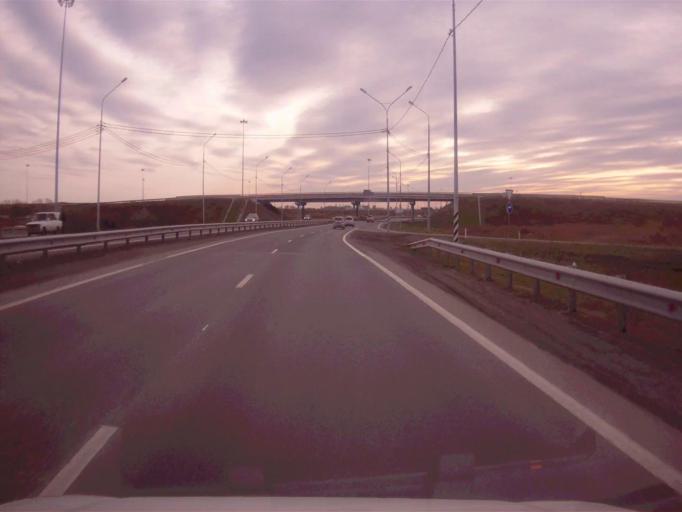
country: RU
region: Chelyabinsk
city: Novosineglazovskiy
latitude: 55.0037
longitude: 61.4540
